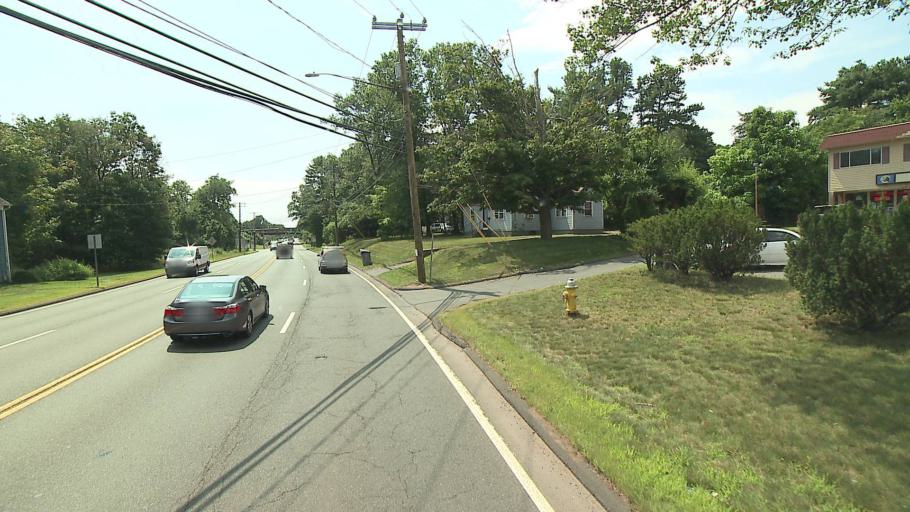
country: US
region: Connecticut
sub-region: Hartford County
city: Plainville
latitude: 41.6797
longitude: -72.8776
